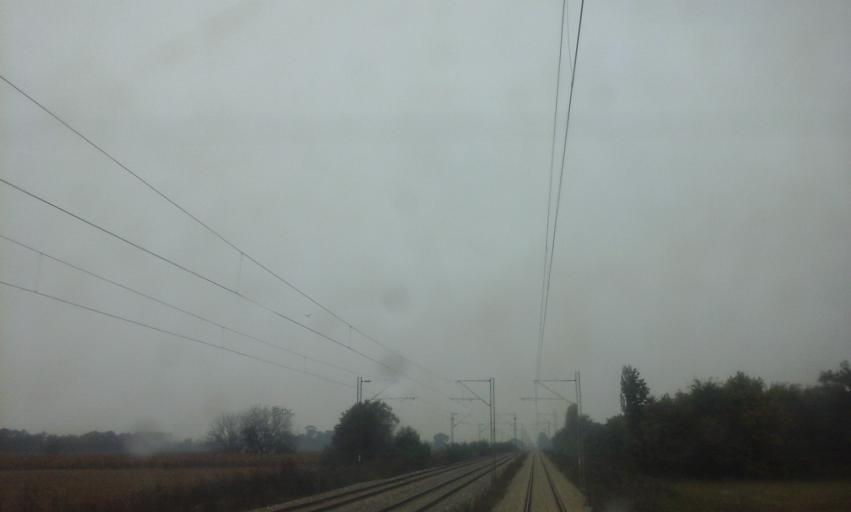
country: RS
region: Central Serbia
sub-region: Pomoravski Okrug
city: Paracin
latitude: 43.8762
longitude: 21.3906
